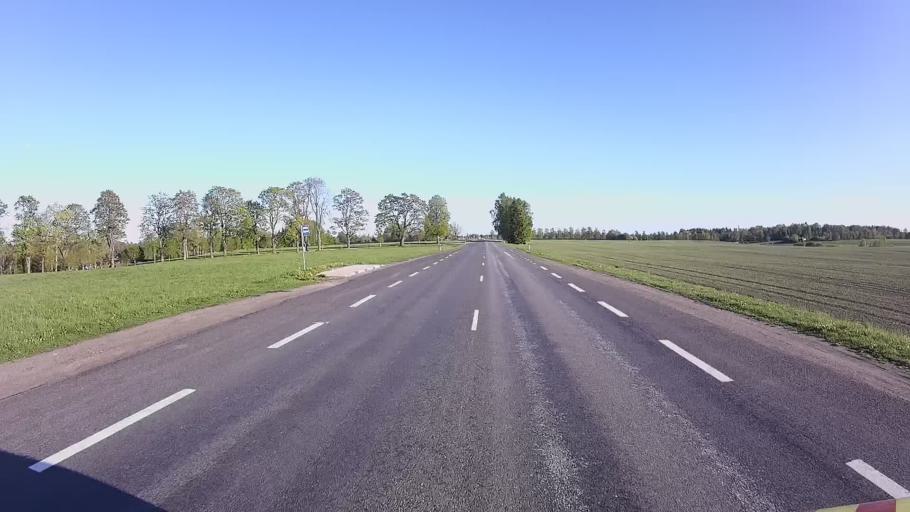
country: EE
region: Viljandimaa
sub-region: Viljandi linn
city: Viljandi
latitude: 58.3963
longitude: 25.5919
